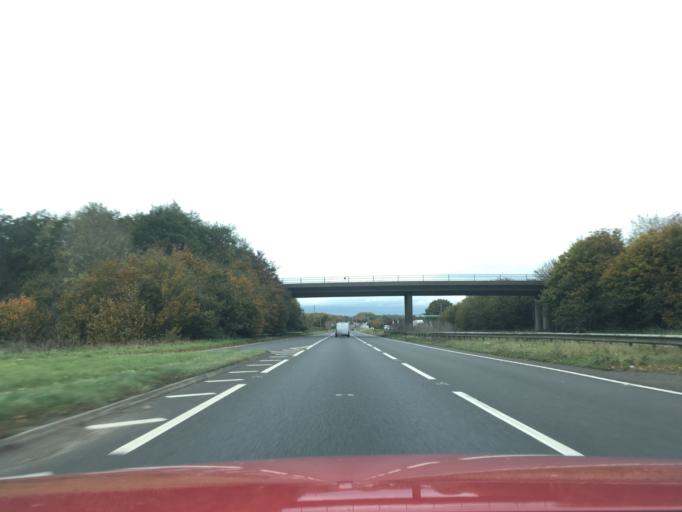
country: GB
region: England
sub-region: Somerset
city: Stoke-sub-Hamdon
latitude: 50.9607
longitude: -2.7544
